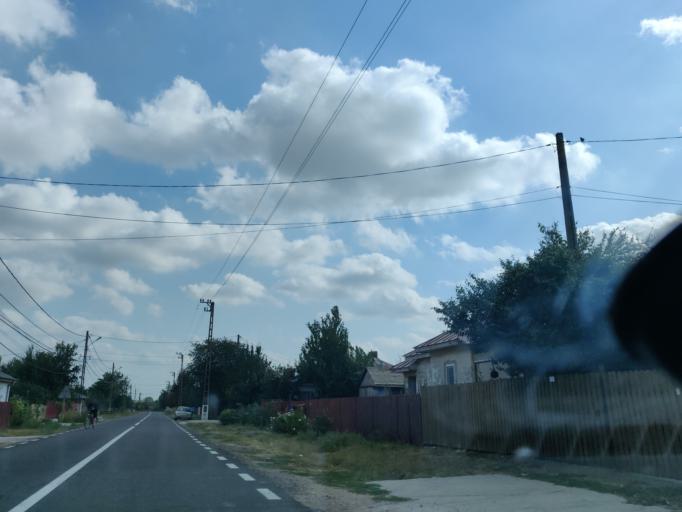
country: RO
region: Vrancea
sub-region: Comuna Ciorasti
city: Ciorasti
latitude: 45.4294
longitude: 27.2971
